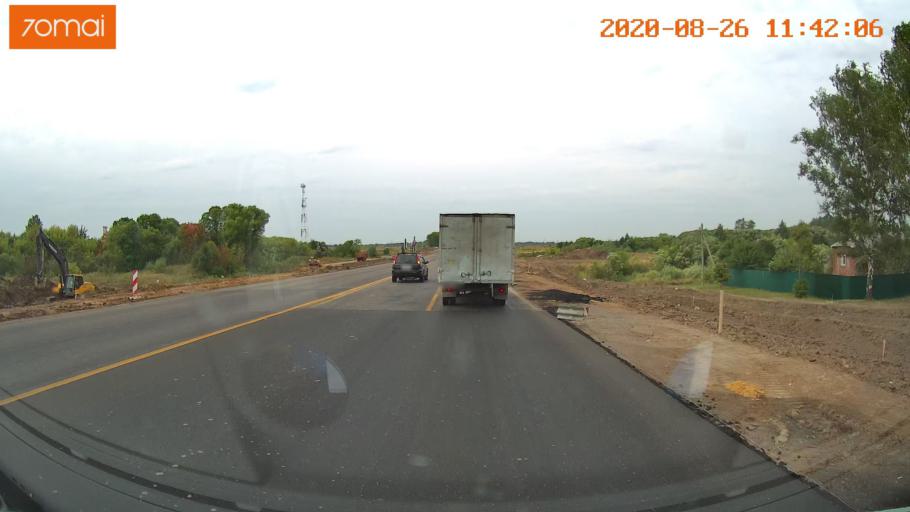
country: RU
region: Rjazan
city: Shilovo
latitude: 54.2964
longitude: 40.6993
